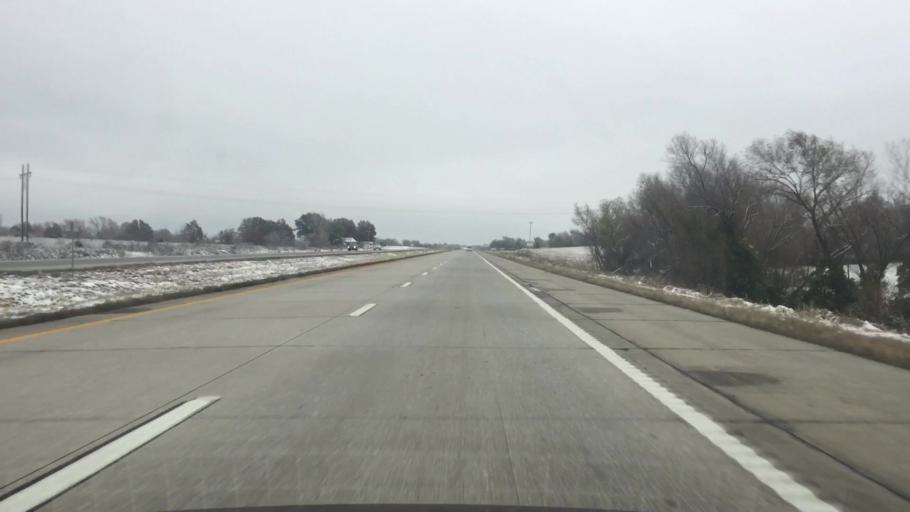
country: US
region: Missouri
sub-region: Saint Clair County
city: Osceola
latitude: 38.1870
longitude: -93.7366
